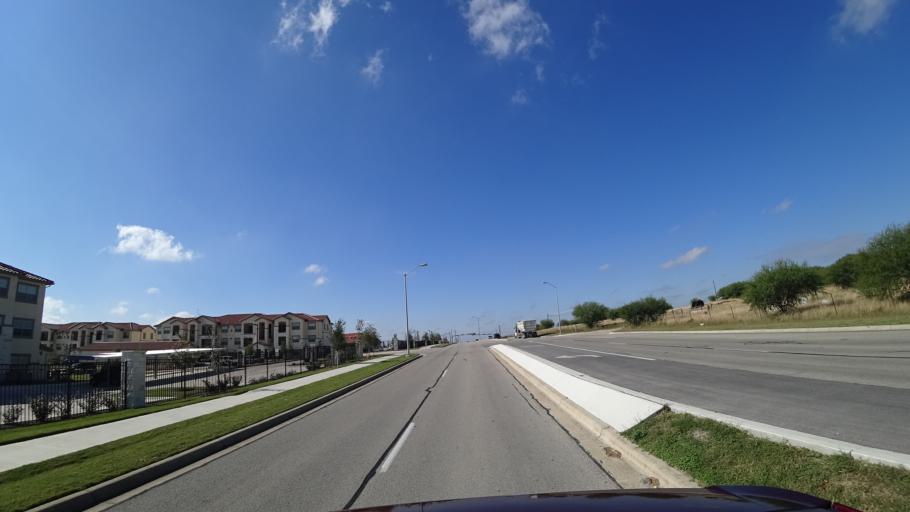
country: US
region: Texas
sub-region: Travis County
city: Windemere
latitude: 30.4334
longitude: -97.6508
